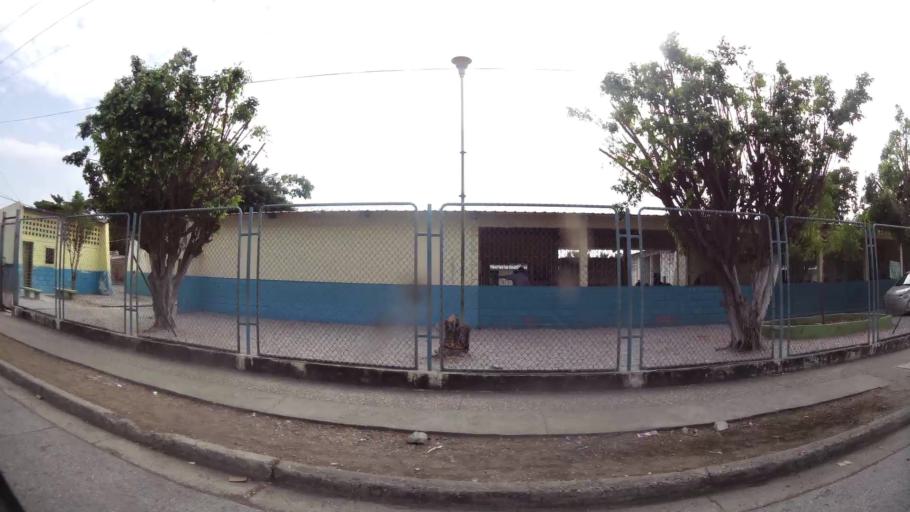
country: EC
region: Guayas
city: Guayaquil
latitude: -2.2524
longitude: -79.8855
